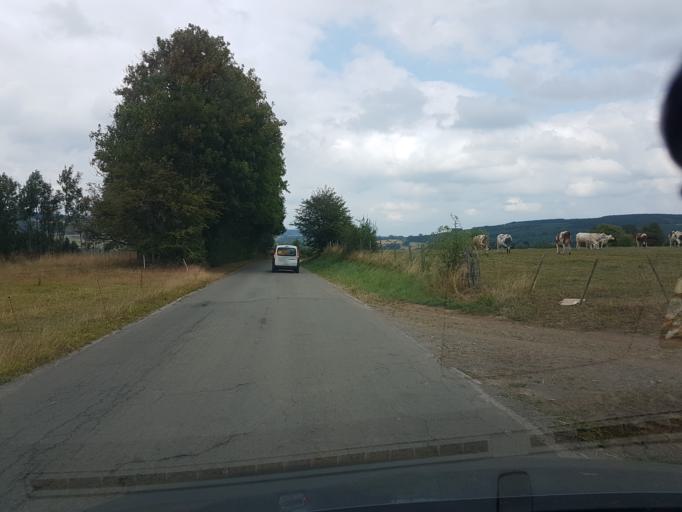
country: BE
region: Wallonia
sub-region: Province du Luxembourg
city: Manhay
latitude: 50.2521
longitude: 5.6447
